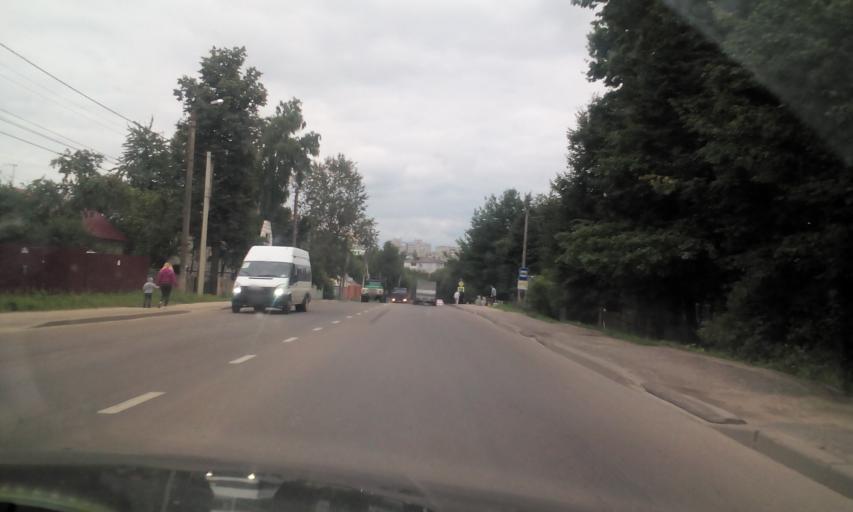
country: RU
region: Kaluga
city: Kaluga
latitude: 54.5149
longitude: 36.3398
